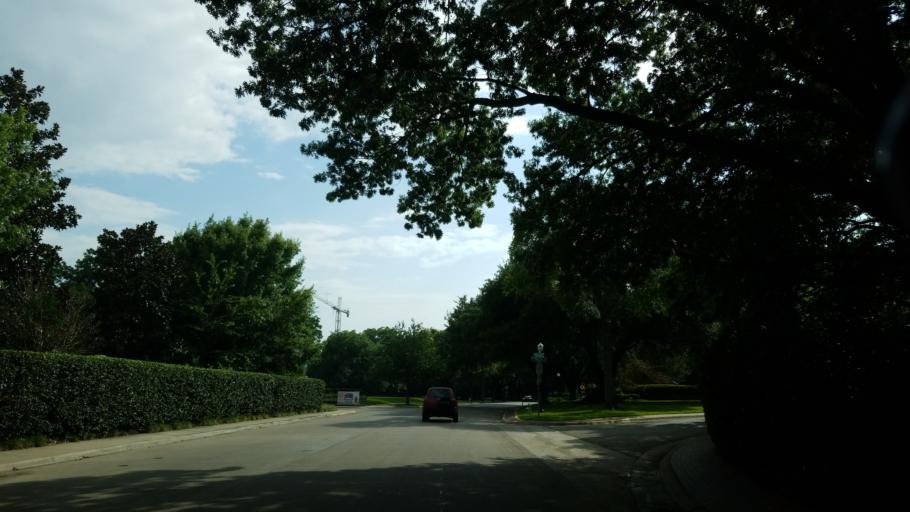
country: US
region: Texas
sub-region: Dallas County
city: University Park
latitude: 32.8475
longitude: -96.7969
